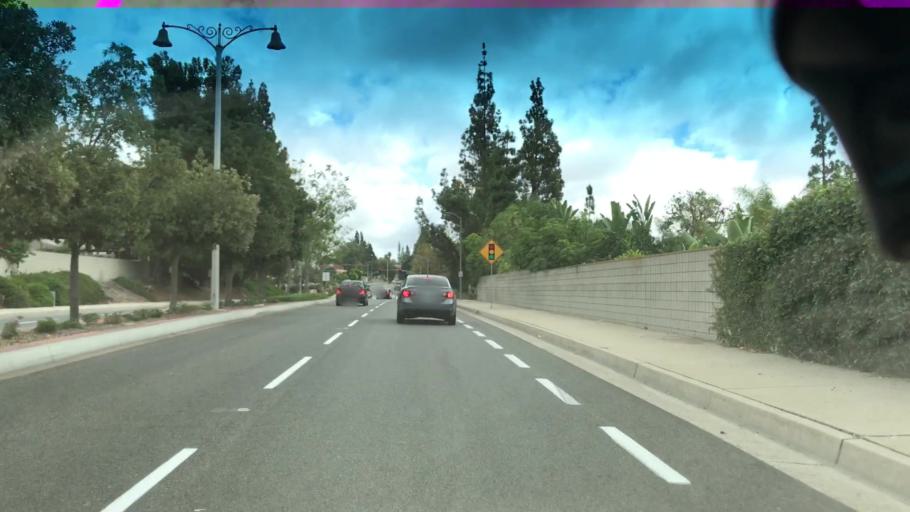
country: US
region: California
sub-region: Orange County
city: Mission Viejo
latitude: 33.6109
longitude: -117.6879
